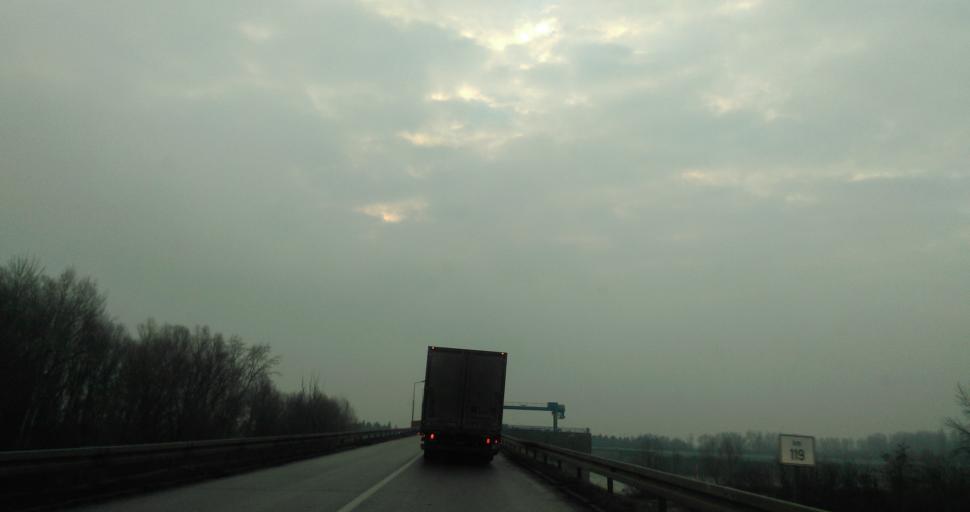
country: RS
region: Autonomna Pokrajina Vojvodina
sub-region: Srednjebanatski Okrug
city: Novi Becej
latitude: 45.5795
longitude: 20.1169
